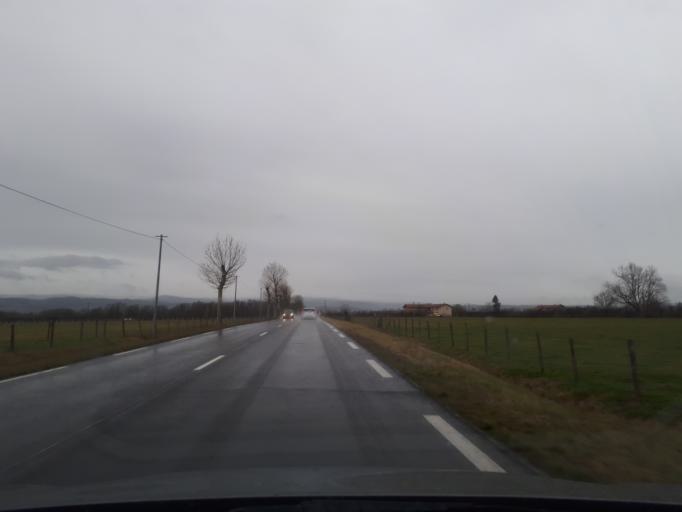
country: FR
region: Rhone-Alpes
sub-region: Departement de la Loire
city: Boen-sur-Lignon
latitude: 45.7381
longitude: 4.1046
